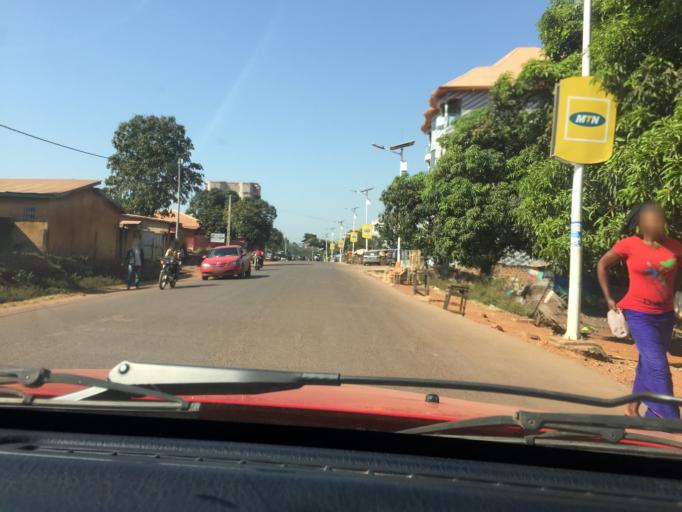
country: GN
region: Labe
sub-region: Labe Prefecture
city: Labe
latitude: 11.3173
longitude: -12.2944
